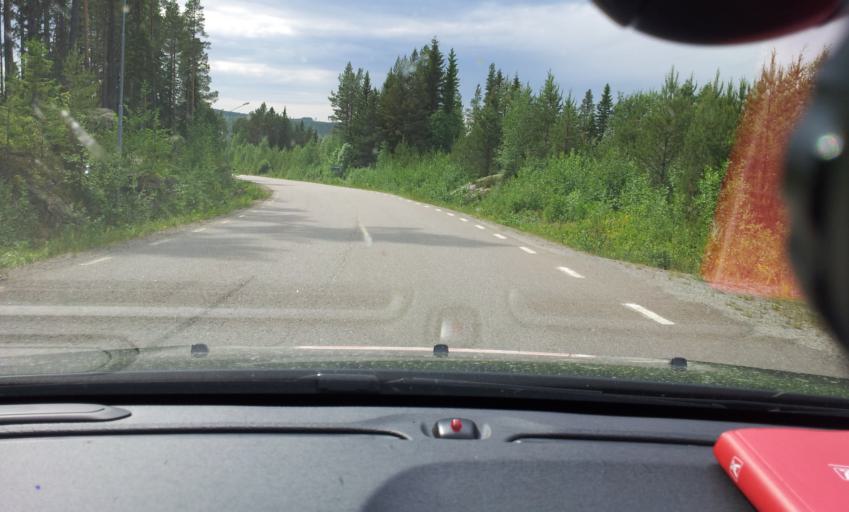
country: SE
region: Jaemtland
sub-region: Bergs Kommun
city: Hoverberg
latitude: 62.6662
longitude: 14.7573
